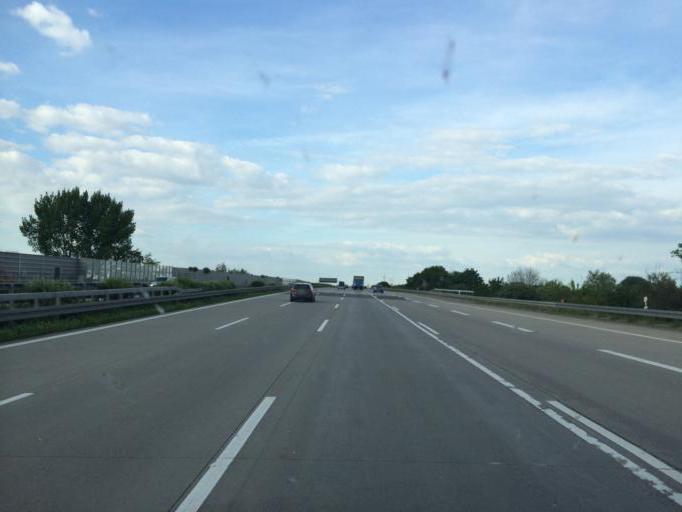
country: DE
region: Saxony-Anhalt
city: Barleben
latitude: 52.1904
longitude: 11.6289
